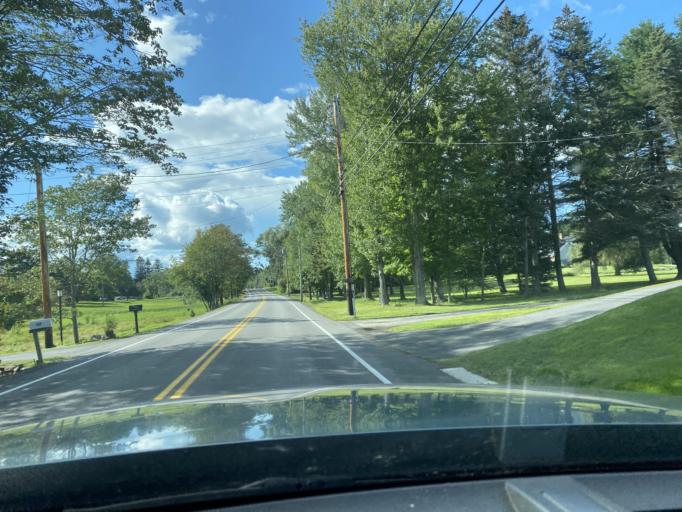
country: US
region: Maine
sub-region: York County
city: Kittery Point
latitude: 43.1434
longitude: -70.7055
